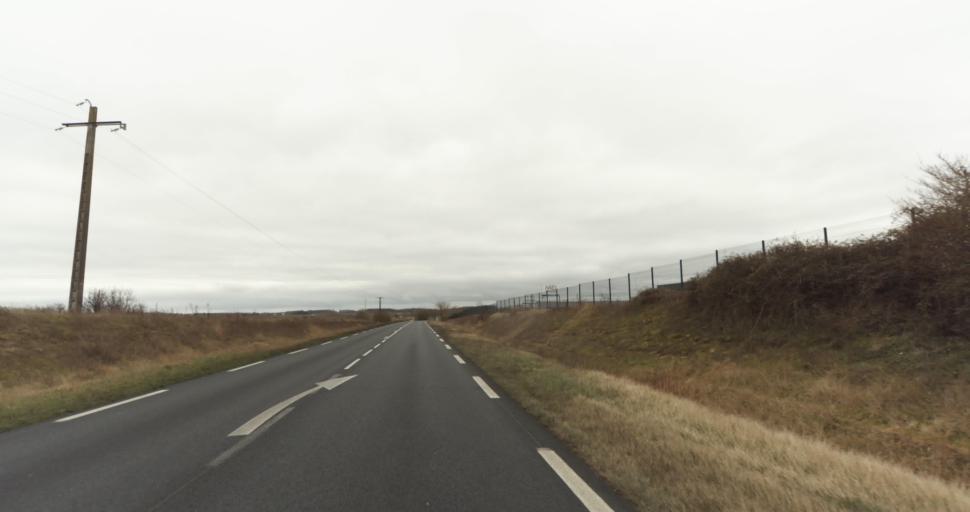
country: FR
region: Pays de la Loire
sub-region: Departement de Maine-et-Loire
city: Doue-la-Fontaine
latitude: 47.1913
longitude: -0.2437
